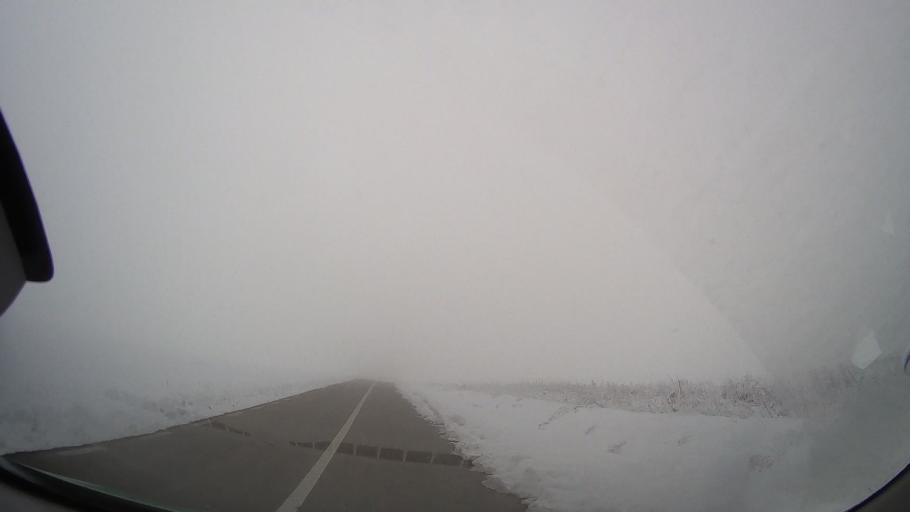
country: RO
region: Iasi
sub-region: Comuna Valea Seaca
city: Topile
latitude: 47.2728
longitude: 26.6704
